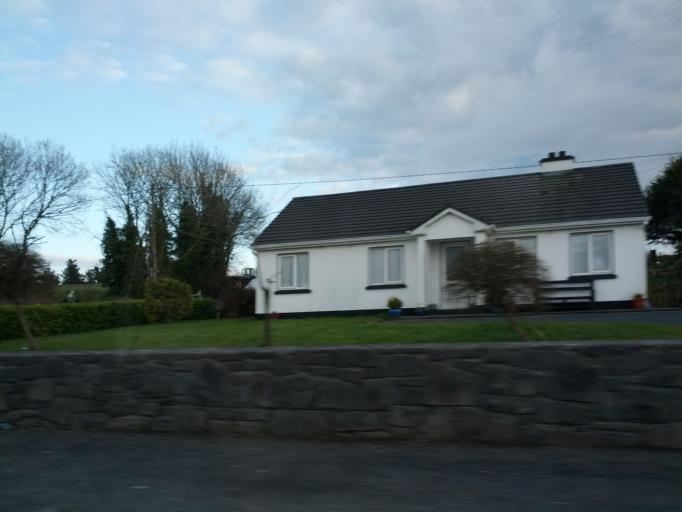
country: IE
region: Connaught
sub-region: County Galway
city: Tuam
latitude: 53.4382
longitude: -8.7348
